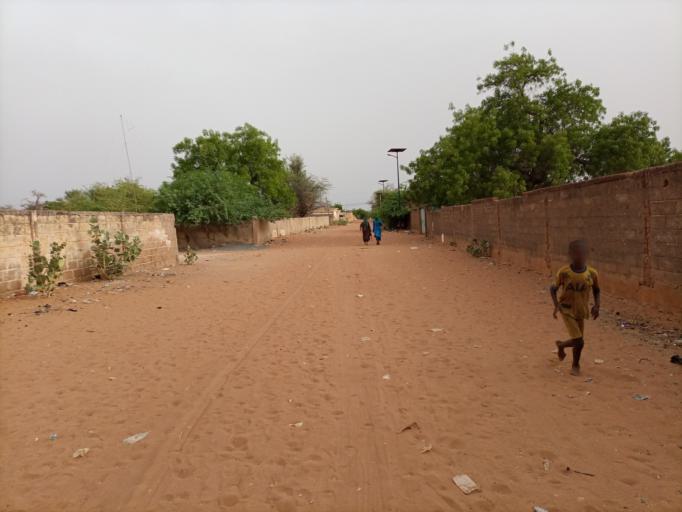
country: SN
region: Louga
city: Ndibene Dahra
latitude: 15.3983
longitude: -15.1144
